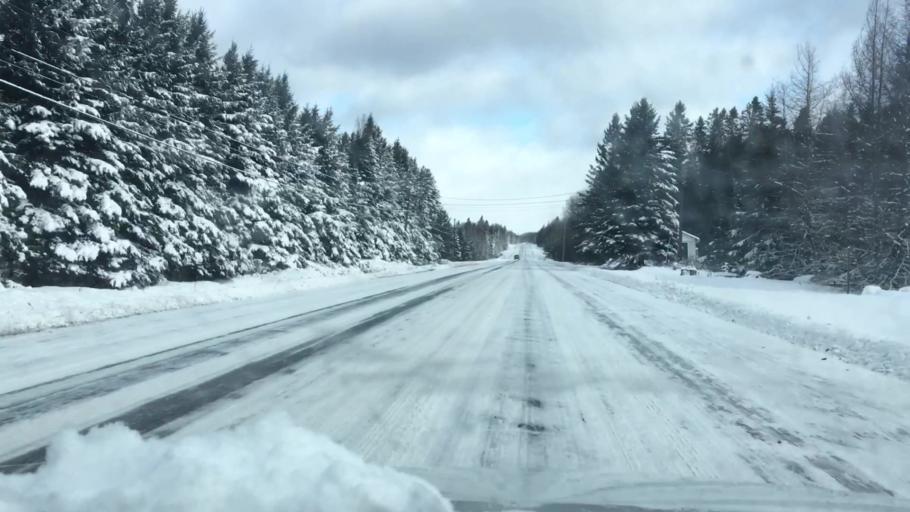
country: US
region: Maine
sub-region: Aroostook County
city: Madawaska
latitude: 47.0189
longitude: -68.0149
